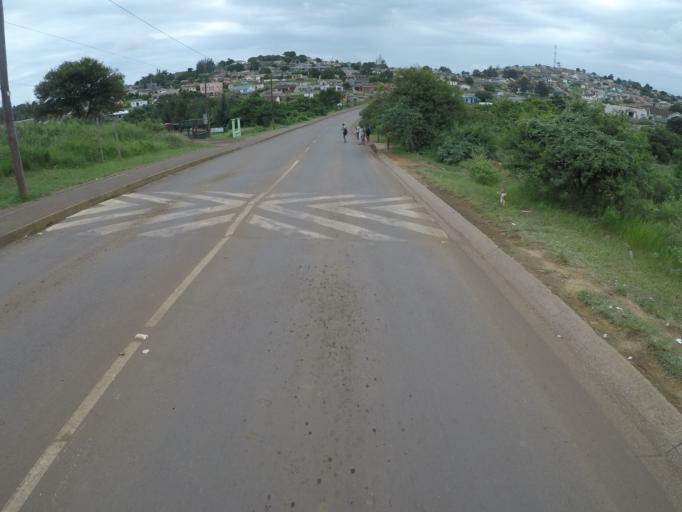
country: ZA
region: KwaZulu-Natal
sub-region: uThungulu District Municipality
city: Empangeni
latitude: -28.7809
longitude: 31.8630
